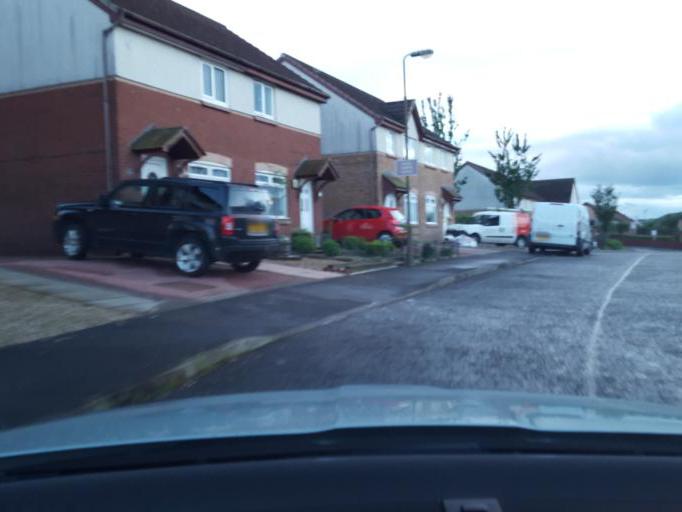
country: GB
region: Scotland
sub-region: West Lothian
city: Armadale
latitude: 55.8972
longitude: -3.7137
